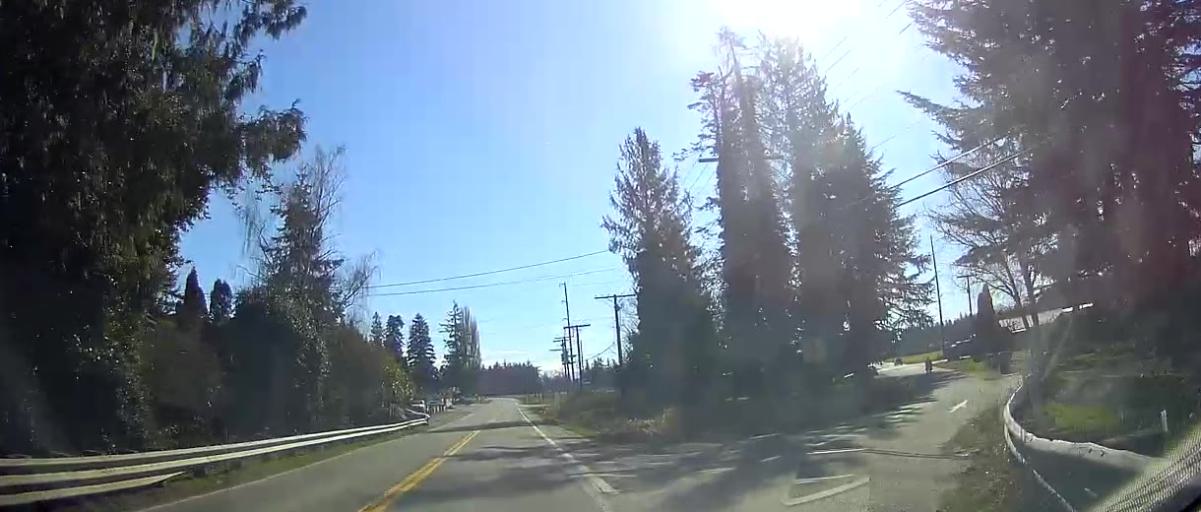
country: US
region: Washington
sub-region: Skagit County
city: Burlington
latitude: 48.5162
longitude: -122.3785
